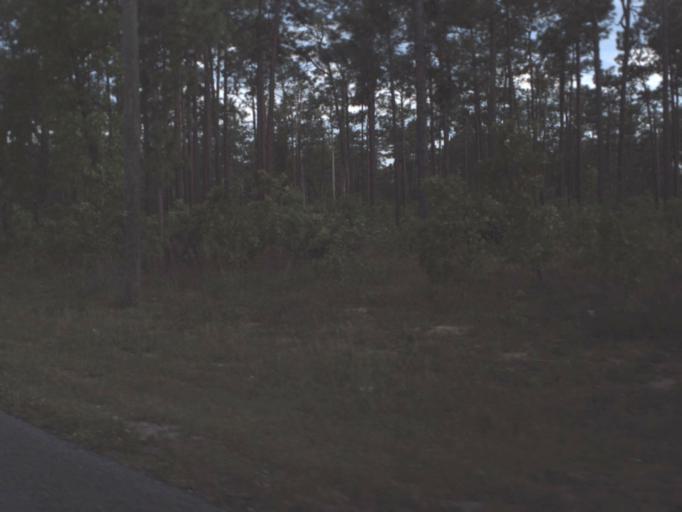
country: US
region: Florida
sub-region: Marion County
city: Silver Springs Shores
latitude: 29.2049
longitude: -81.9403
